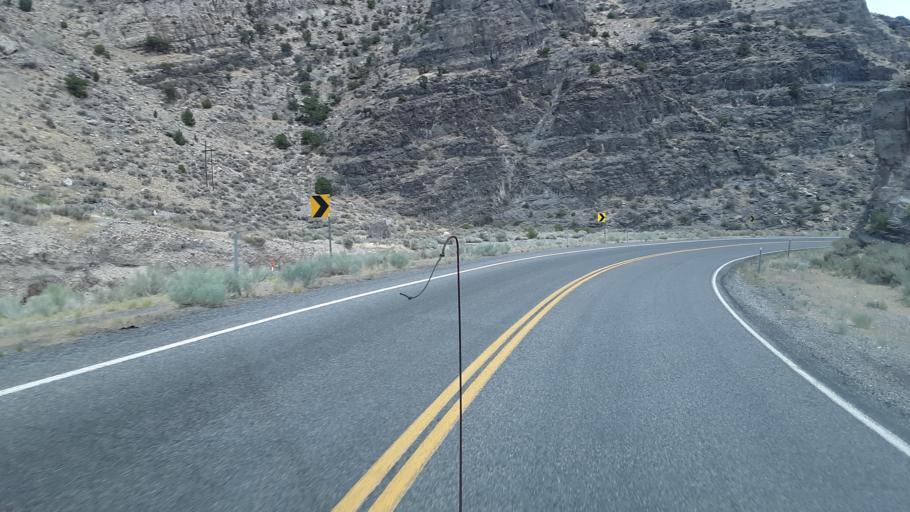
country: US
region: Utah
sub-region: Beaver County
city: Milford
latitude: 39.0870
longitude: -113.5682
